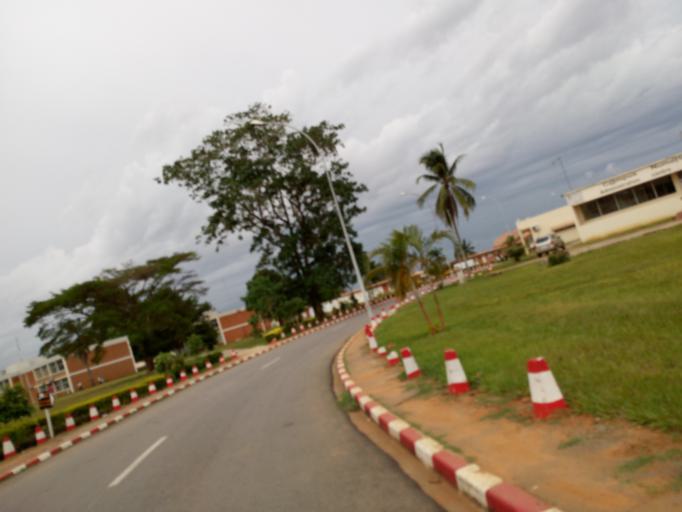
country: CI
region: Lagunes
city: Abidjan
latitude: 5.3434
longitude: -3.9880
